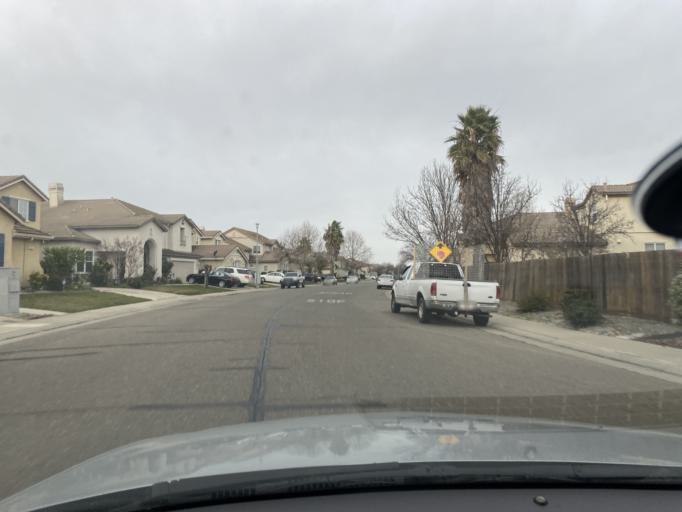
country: US
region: California
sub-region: Sacramento County
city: Elk Grove
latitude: 38.4444
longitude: -121.3884
